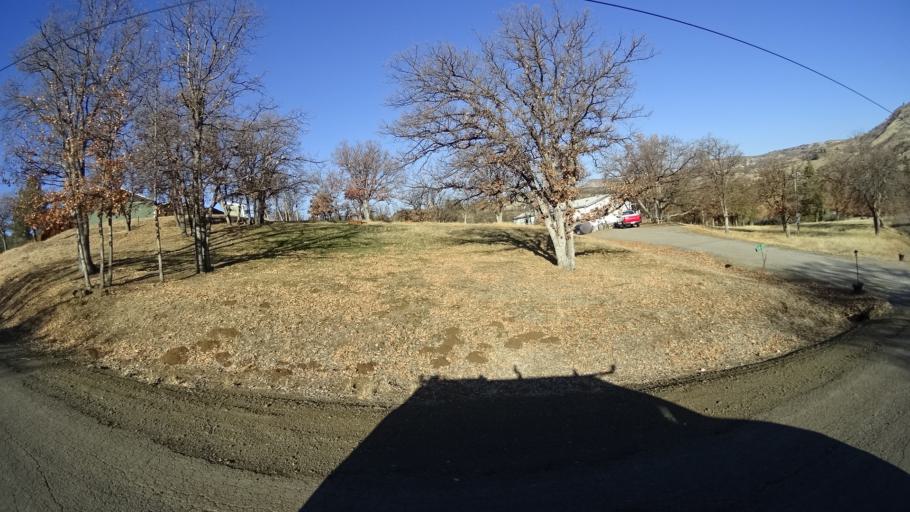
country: US
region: California
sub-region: Siskiyou County
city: Montague
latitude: 41.8946
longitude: -122.5021
